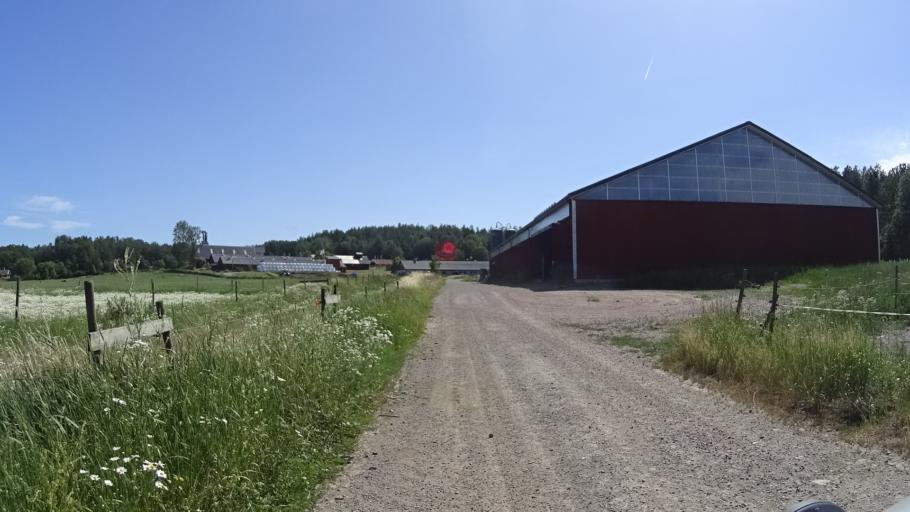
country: SE
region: Kalmar
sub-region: Vasterviks Kommun
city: Gamleby
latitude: 57.9155
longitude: 16.4055
